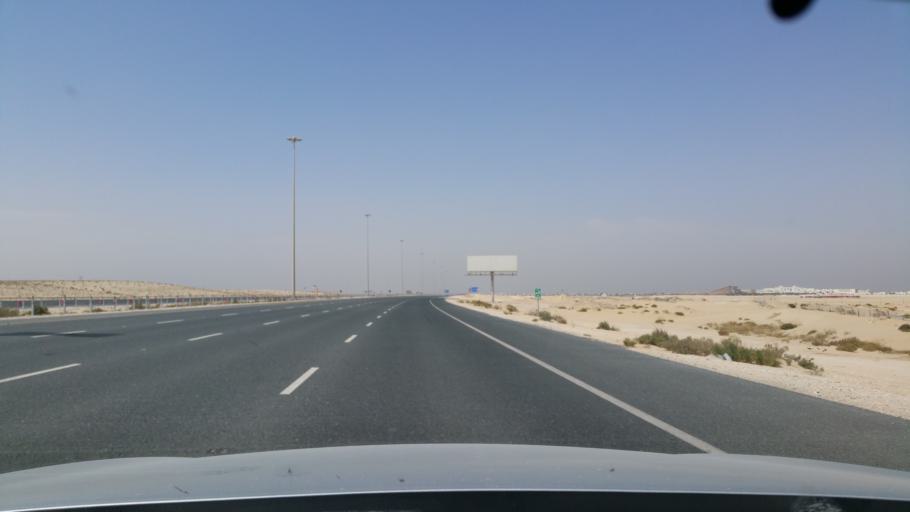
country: QA
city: Umm Bab
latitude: 24.8528
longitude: 50.8894
